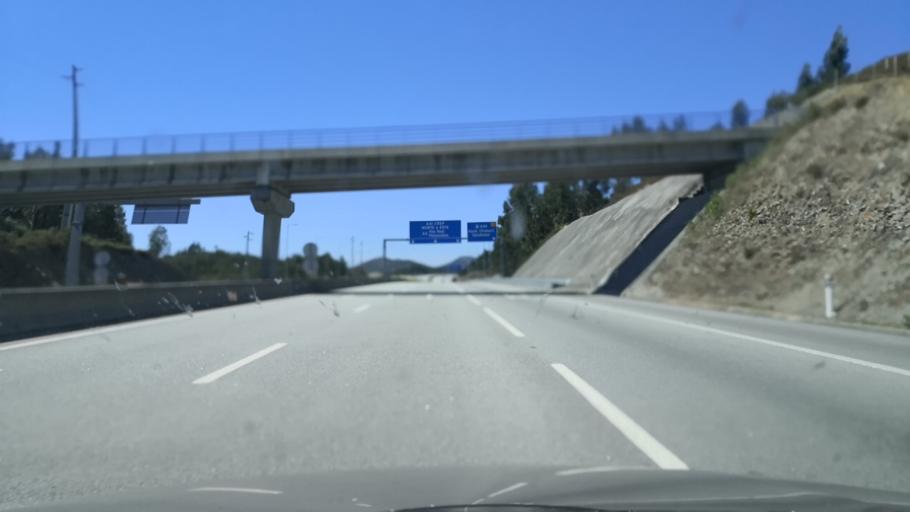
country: PT
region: Porto
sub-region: Gondomar
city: Foz do Sousa
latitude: 41.0887
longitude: -8.4551
